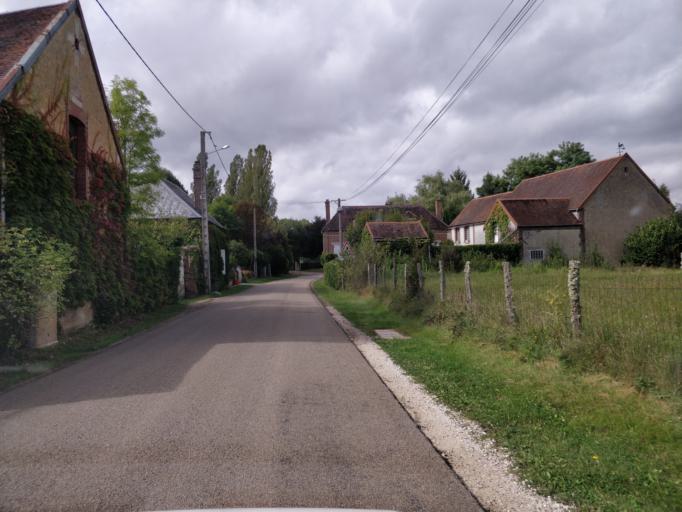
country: FR
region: Champagne-Ardenne
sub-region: Departement de l'Aube
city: Aix-en-Othe
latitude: 48.1495
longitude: 3.6428
